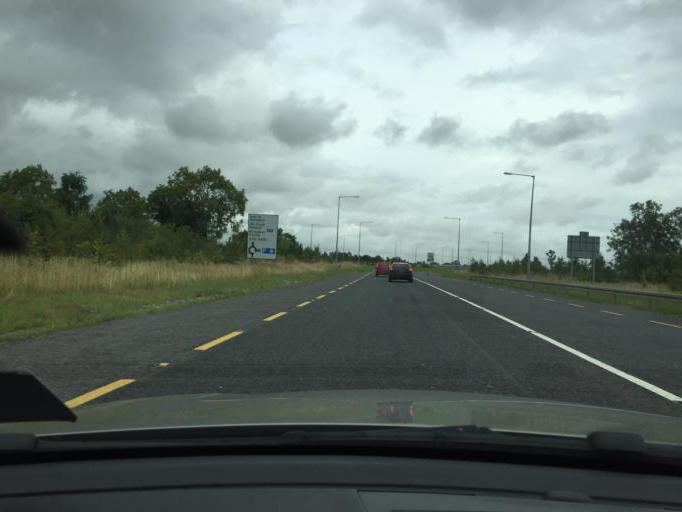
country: IE
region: Leinster
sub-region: An Mhi
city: Dunboyne
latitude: 53.4334
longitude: -6.4752
